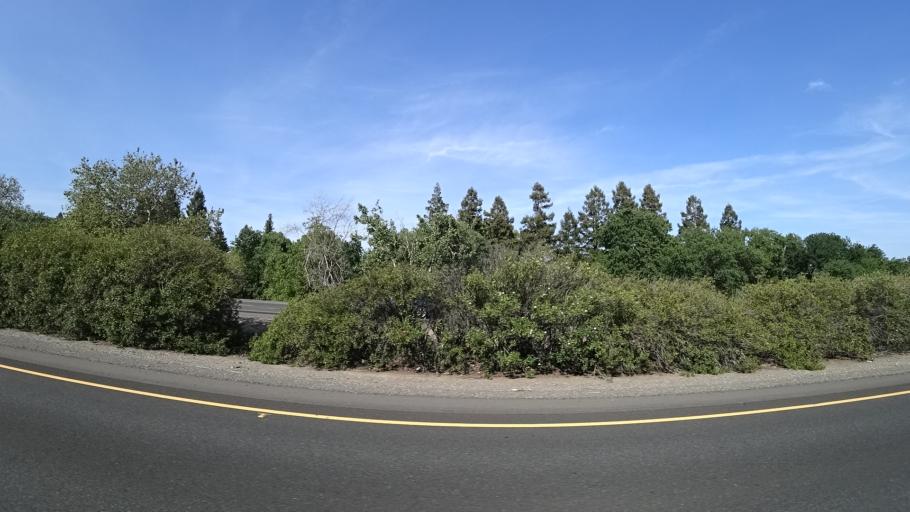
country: US
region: California
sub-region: Butte County
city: Chico
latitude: 39.7635
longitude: -121.8600
